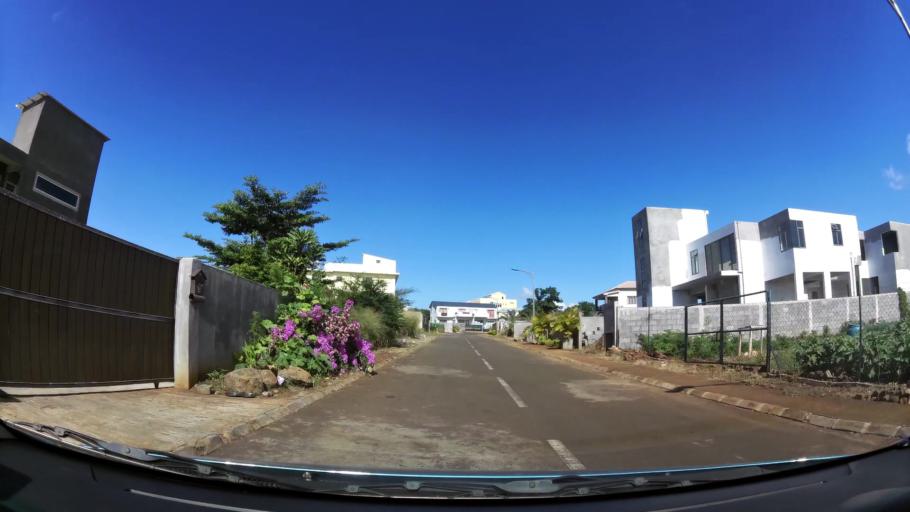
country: MU
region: Black River
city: Albion
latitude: -20.2169
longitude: 57.4153
